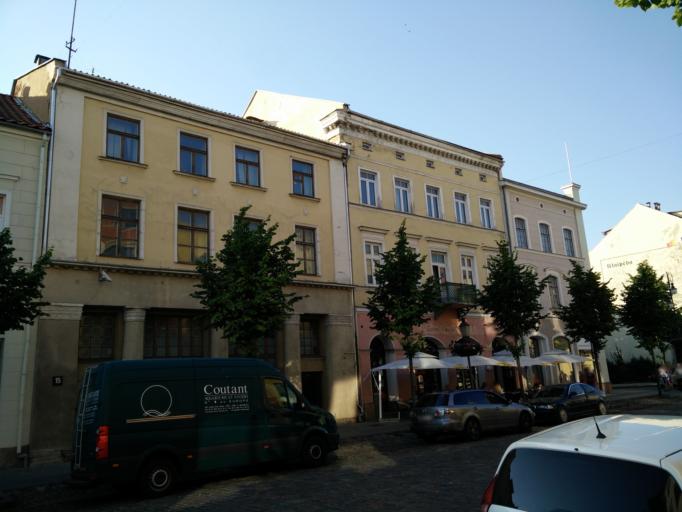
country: LT
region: Klaipedos apskritis
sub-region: Klaipeda
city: Klaipeda
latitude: 55.7086
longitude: 21.1347
